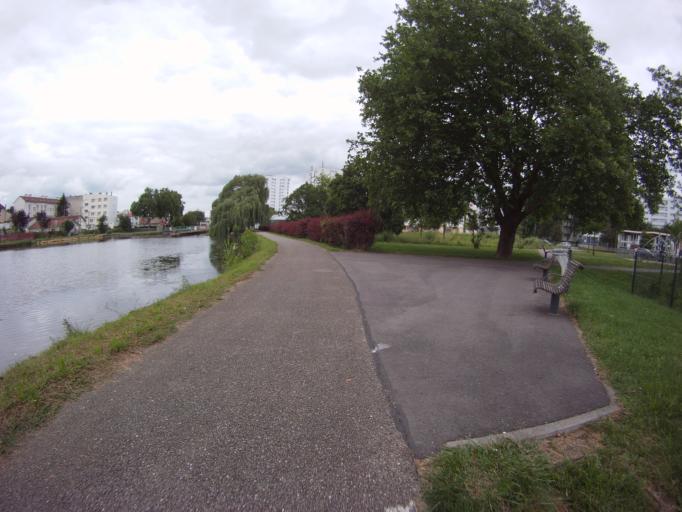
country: FR
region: Lorraine
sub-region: Departement de Meurthe-et-Moselle
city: Jarville-la-Malgrange
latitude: 48.6711
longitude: 6.2081
